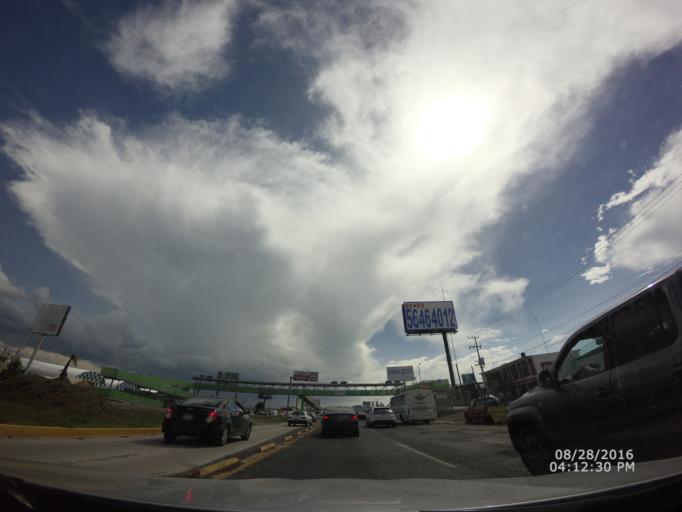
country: CN
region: Xinjiang Uygur Zizhiqu
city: Oytograk
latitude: 37.4850
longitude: 81.9519
